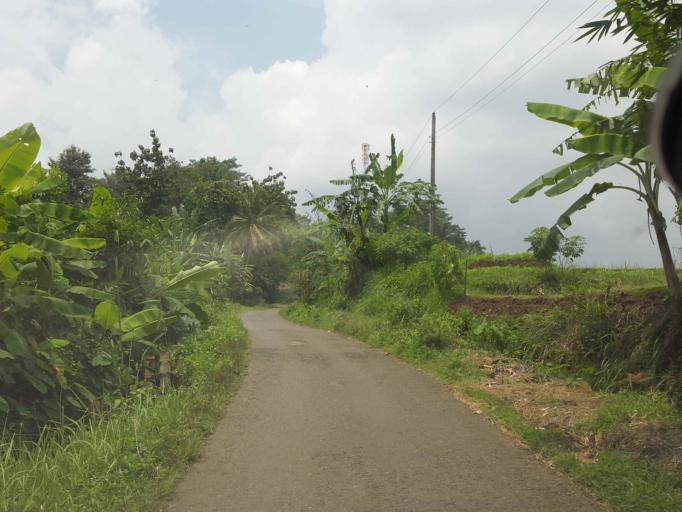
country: ID
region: Central Java
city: Muara
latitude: -7.2880
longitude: 108.9863
